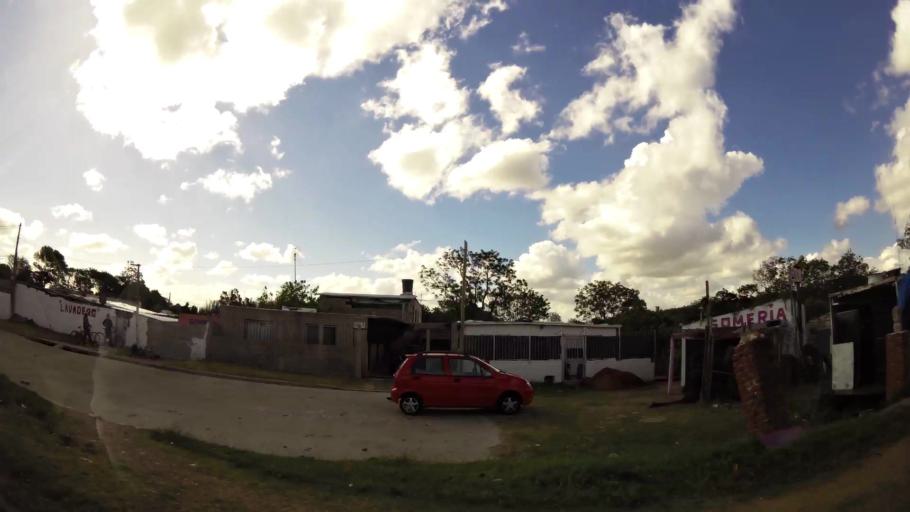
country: UY
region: Canelones
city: La Paz
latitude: -34.8100
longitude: -56.2267
